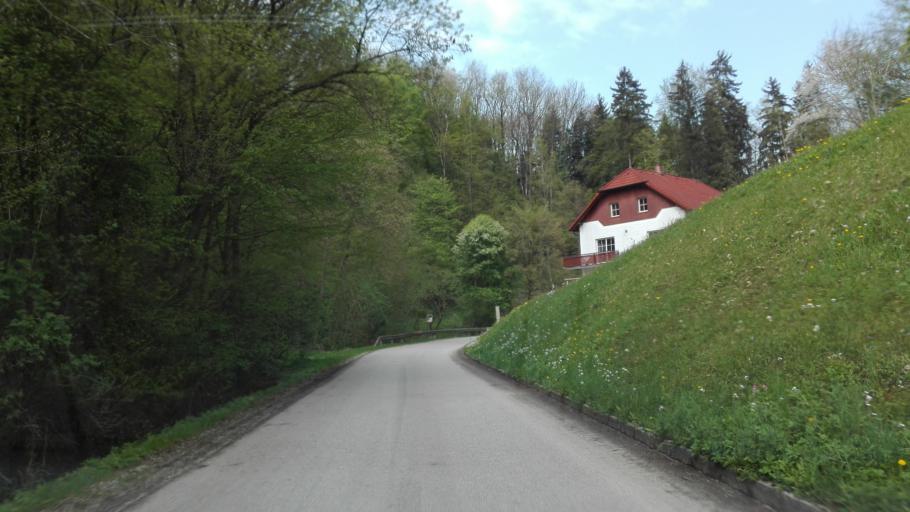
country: AT
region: Upper Austria
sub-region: Politischer Bezirk Perg
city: Bad Kreuzen
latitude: 48.2267
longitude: 14.7282
